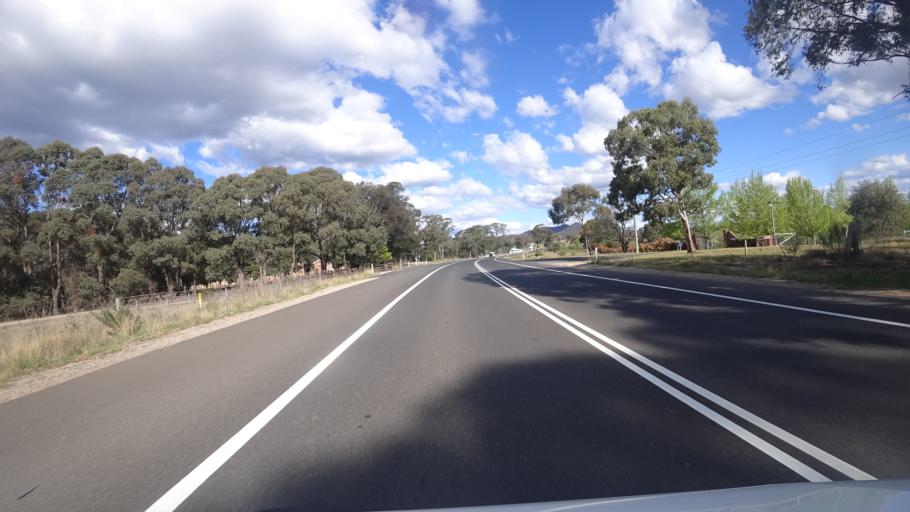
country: AU
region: New South Wales
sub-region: Lithgow
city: Bowenfels
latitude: -33.5564
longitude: 150.1923
